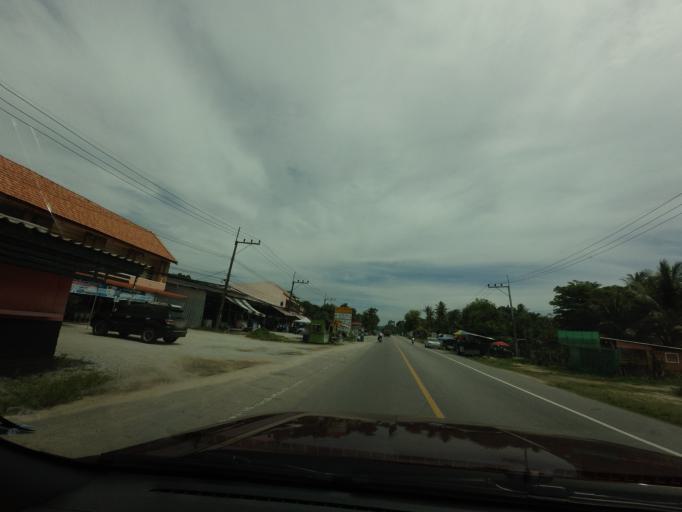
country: TH
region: Narathiwat
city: Tak Bai
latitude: 6.2570
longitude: 102.0481
